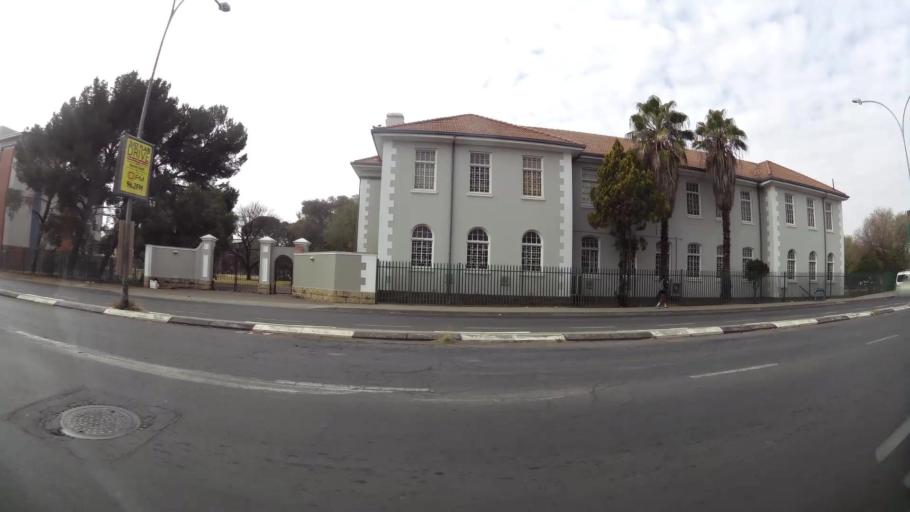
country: ZA
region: Orange Free State
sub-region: Mangaung Metropolitan Municipality
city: Bloemfontein
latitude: -29.1232
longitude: 26.2115
